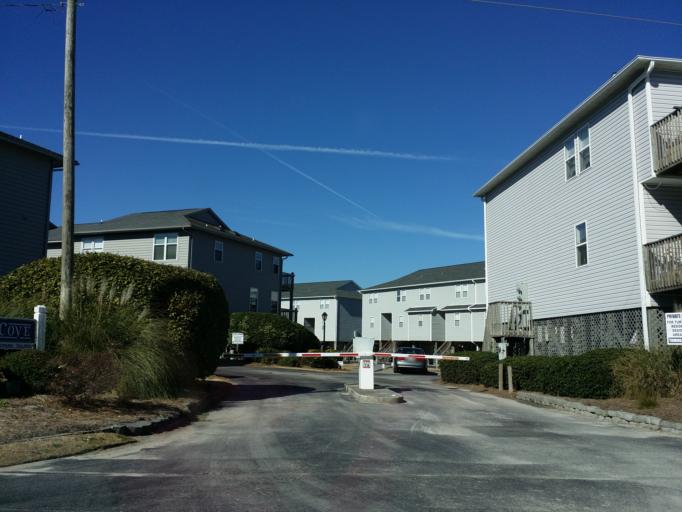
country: US
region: North Carolina
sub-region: Pender County
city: Surf City
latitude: 34.4198
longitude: -77.5548
